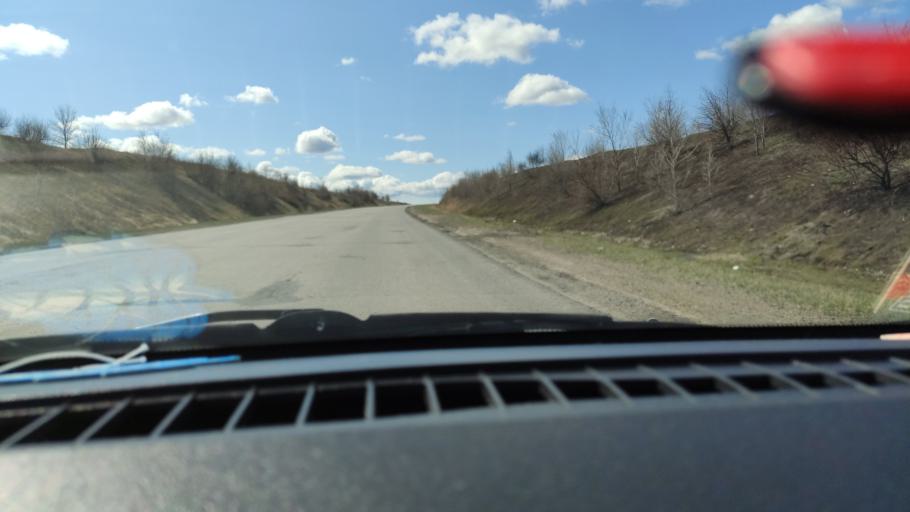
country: RU
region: Samara
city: Varlamovo
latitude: 53.0621
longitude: 48.3520
